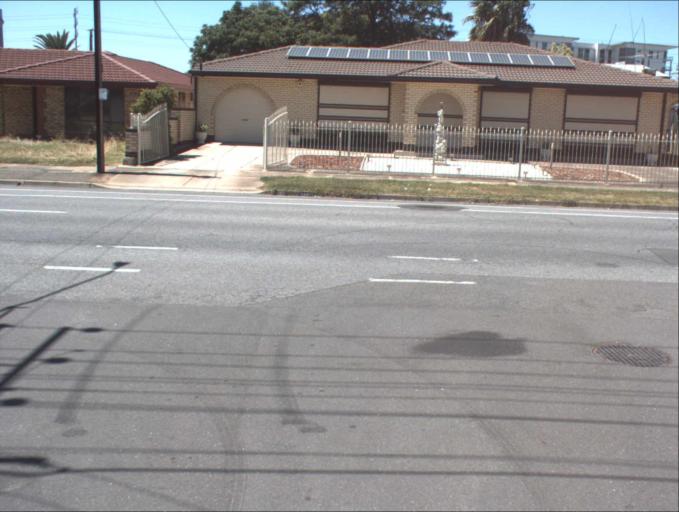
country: AU
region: South Australia
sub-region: Port Adelaide Enfield
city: Birkenhead
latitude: -34.8442
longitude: 138.4919
